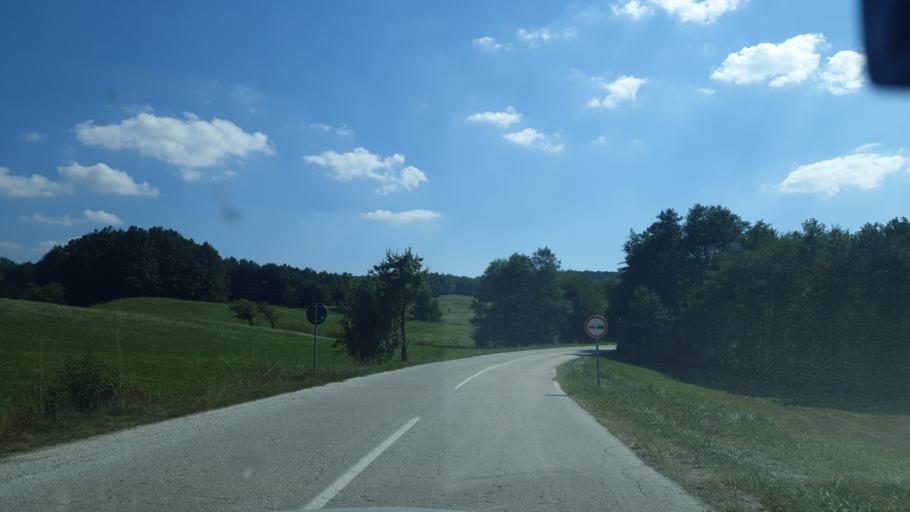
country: RS
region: Central Serbia
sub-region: Zlatiborski Okrug
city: Kosjeric
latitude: 44.0441
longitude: 20.0220
